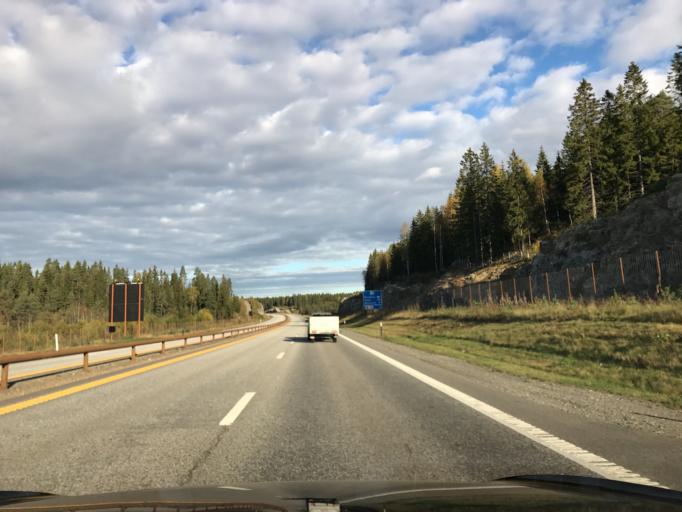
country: NO
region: Akershus
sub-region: Eidsvoll
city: Raholt
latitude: 60.2607
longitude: 11.1747
